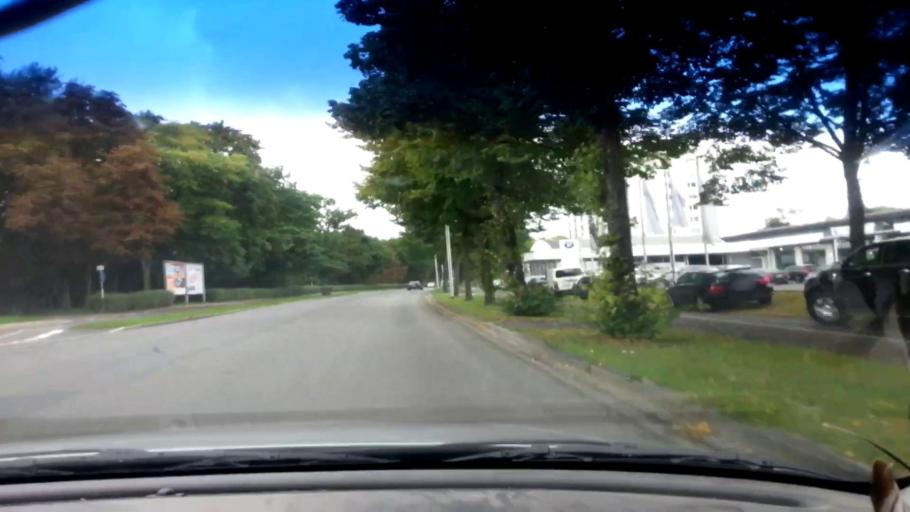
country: DE
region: Bavaria
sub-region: Upper Franconia
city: Bamberg
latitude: 49.8867
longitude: 10.9070
